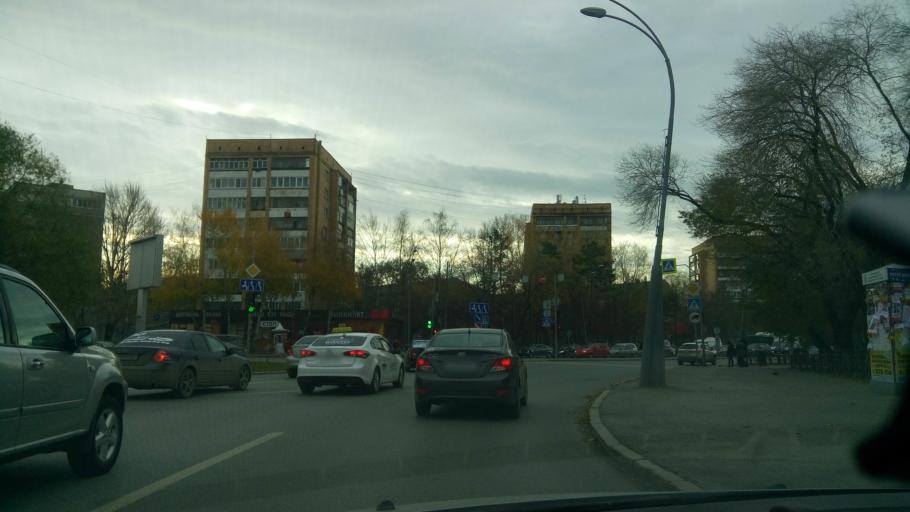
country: RU
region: Tjumen
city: Tyumen
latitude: 57.1455
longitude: 65.5808
